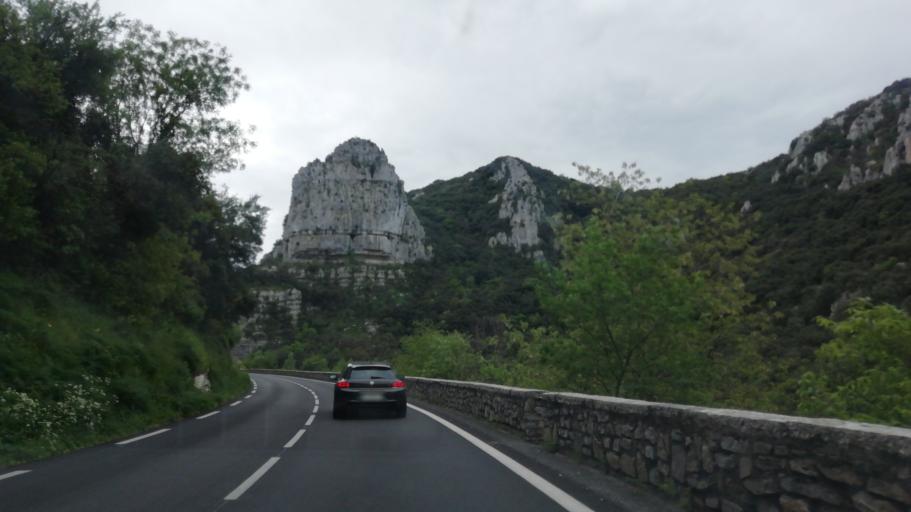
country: FR
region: Languedoc-Roussillon
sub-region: Departement de l'Herault
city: Laroque
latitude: 43.9120
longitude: 3.7369
